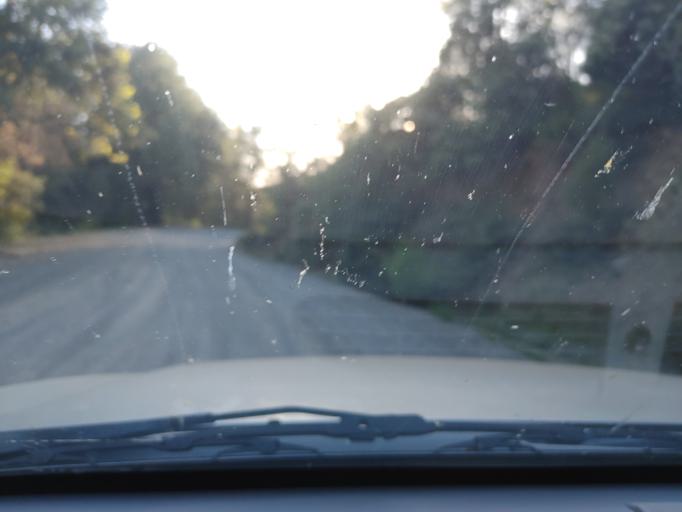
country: US
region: California
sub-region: Shasta County
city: Bella Vista
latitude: 40.8222
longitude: -122.0157
